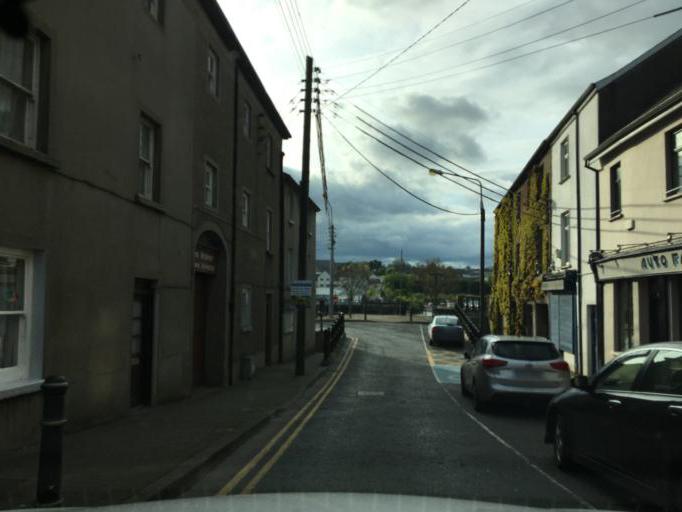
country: IE
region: Leinster
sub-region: Loch Garman
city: New Ross
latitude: 52.3966
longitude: -6.9443
